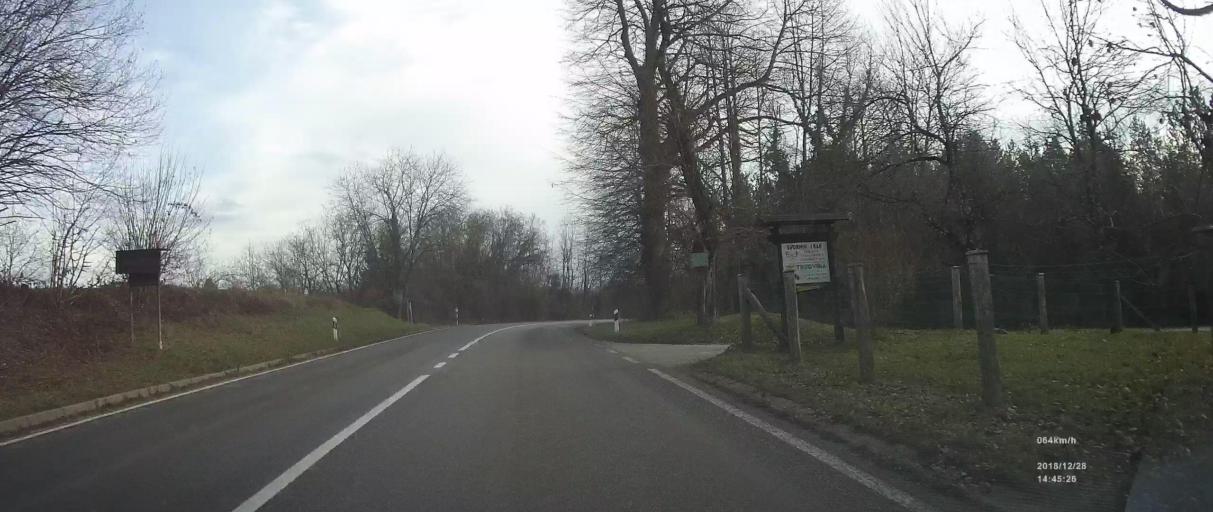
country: SI
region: Crnomelj
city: Crnomelj
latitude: 45.4525
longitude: 15.3044
